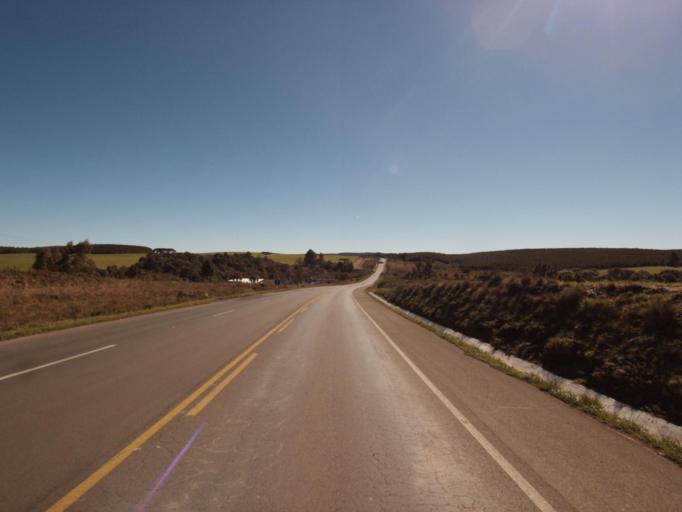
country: BR
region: Santa Catarina
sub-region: Concordia
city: Concordia
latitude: -26.9325
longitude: -51.8727
